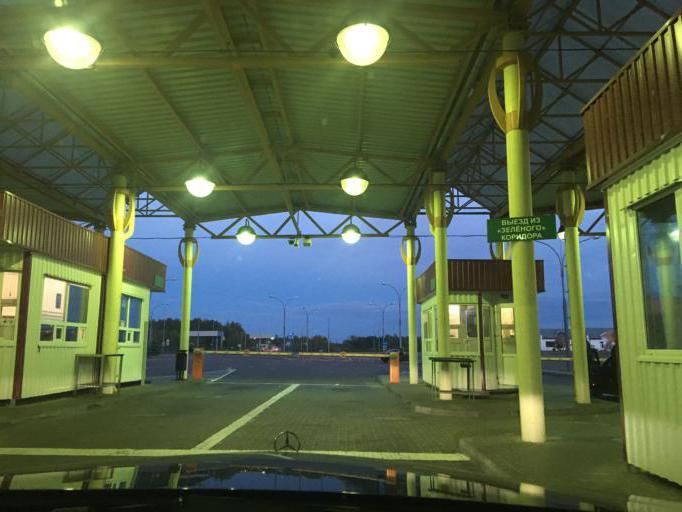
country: PL
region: Lublin Voivodeship
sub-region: Powiat bialski
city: Slawatycze
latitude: 51.7633
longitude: 23.6004
